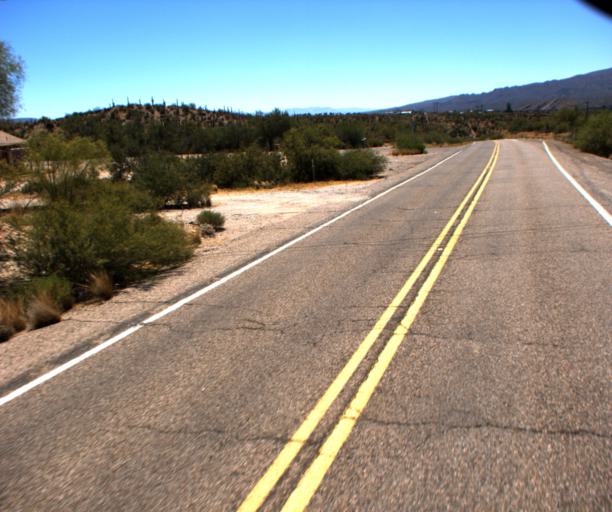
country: US
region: Arizona
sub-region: Pinal County
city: Kearny
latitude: 33.0776
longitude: -110.9235
